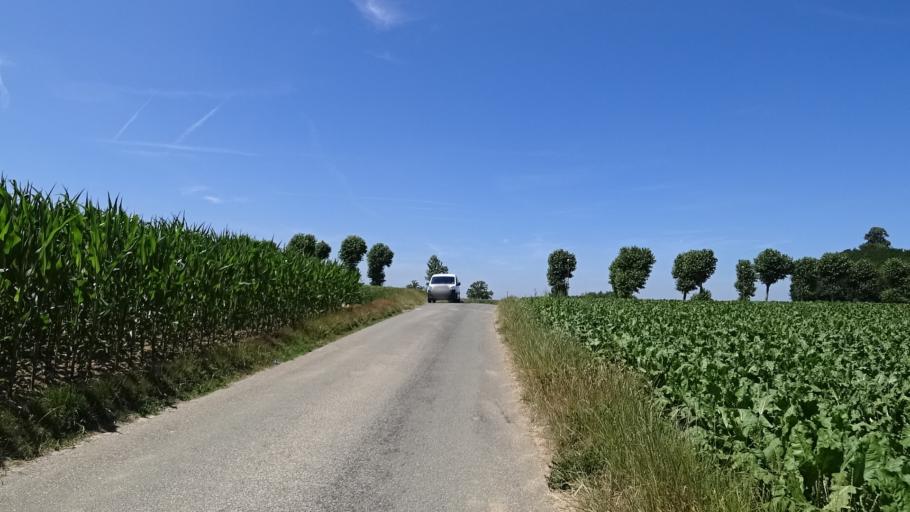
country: BE
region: Wallonia
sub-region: Province du Brabant Wallon
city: Incourt
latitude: 50.6751
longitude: 4.8324
